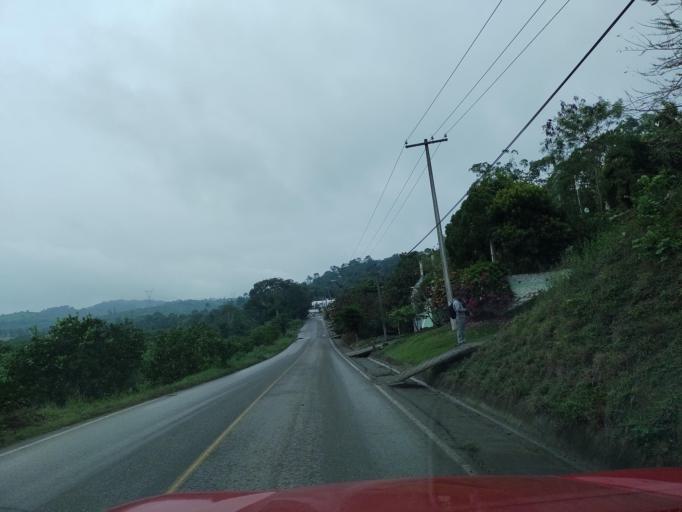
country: MX
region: Puebla
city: Espinal
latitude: 20.2620
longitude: -97.3675
